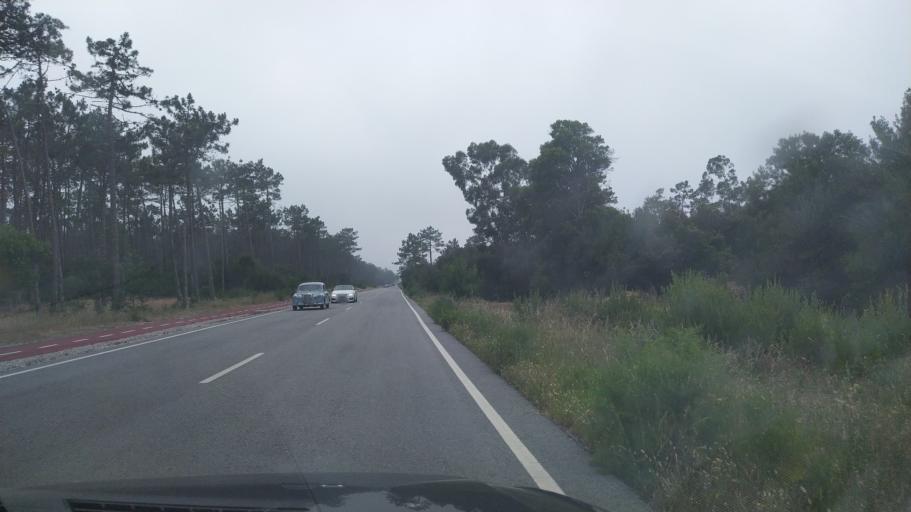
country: PT
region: Aveiro
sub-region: Ilhavo
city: Gafanha da Encarnacao
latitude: 40.5663
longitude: -8.7401
